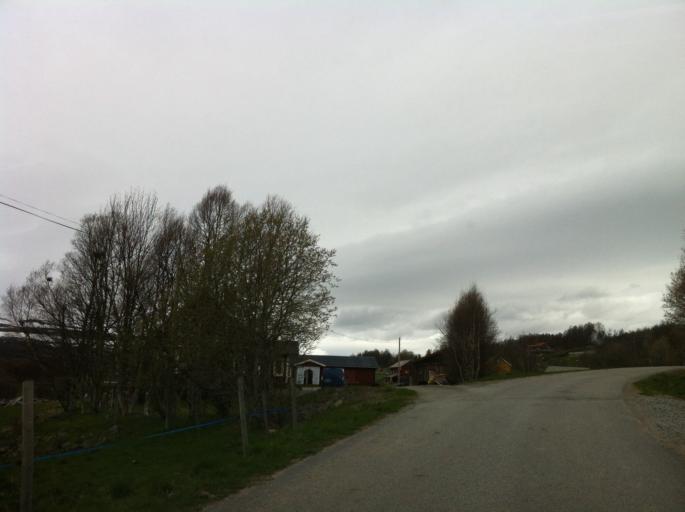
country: NO
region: Sor-Trondelag
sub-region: Tydal
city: Aas
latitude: 62.6314
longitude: 12.4451
